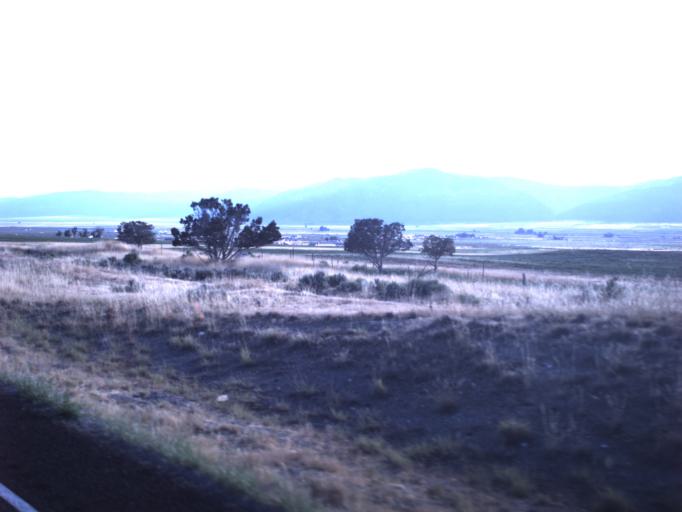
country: US
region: Utah
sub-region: Sanpete County
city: Moroni
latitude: 39.4689
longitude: -111.5315
